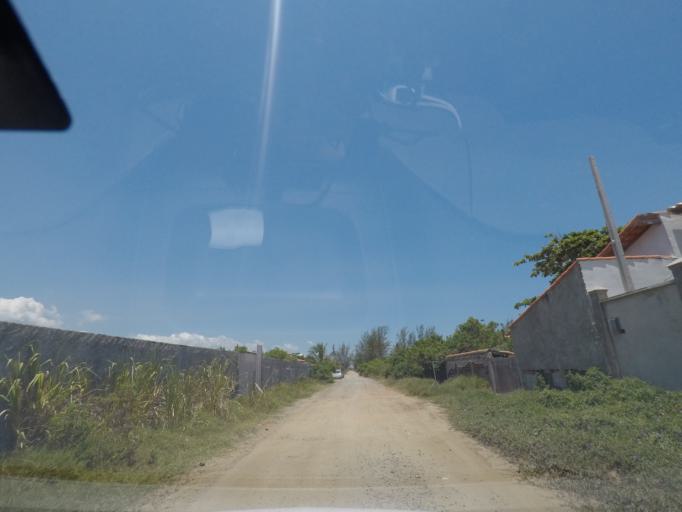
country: BR
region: Rio de Janeiro
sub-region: Niteroi
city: Niteroi
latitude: -22.9683
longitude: -42.9874
